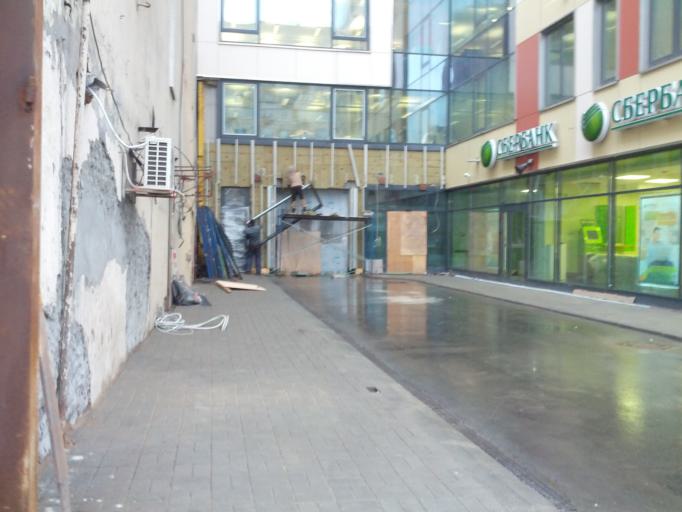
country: RU
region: St.-Petersburg
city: Centralniy
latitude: 59.9139
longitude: 30.3502
